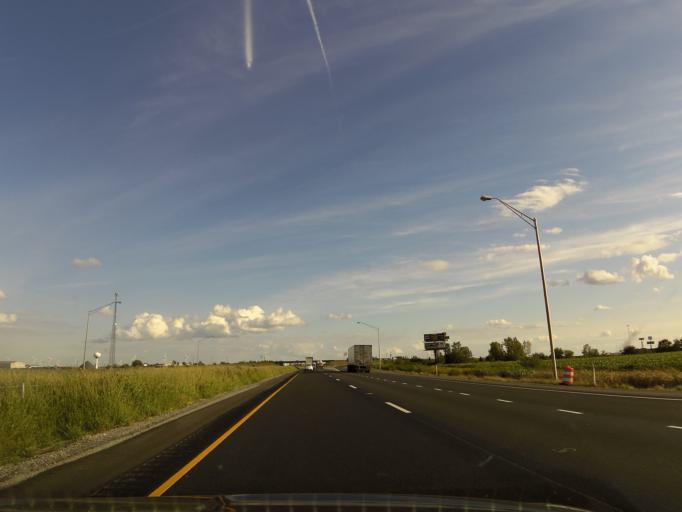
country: US
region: Indiana
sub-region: Jasper County
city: Remington
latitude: 40.7709
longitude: -87.1230
